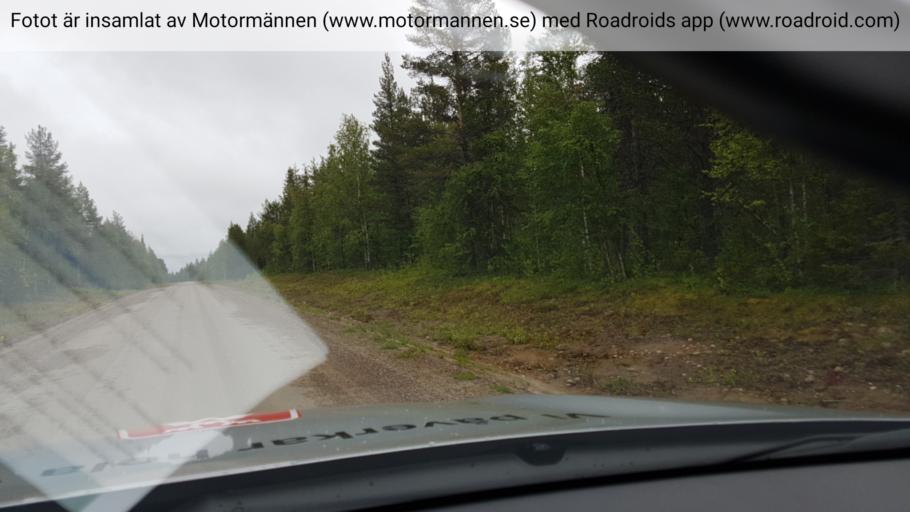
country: SE
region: Norrbotten
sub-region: Gallivare Kommun
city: Gaellivare
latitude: 66.7411
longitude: 20.8738
